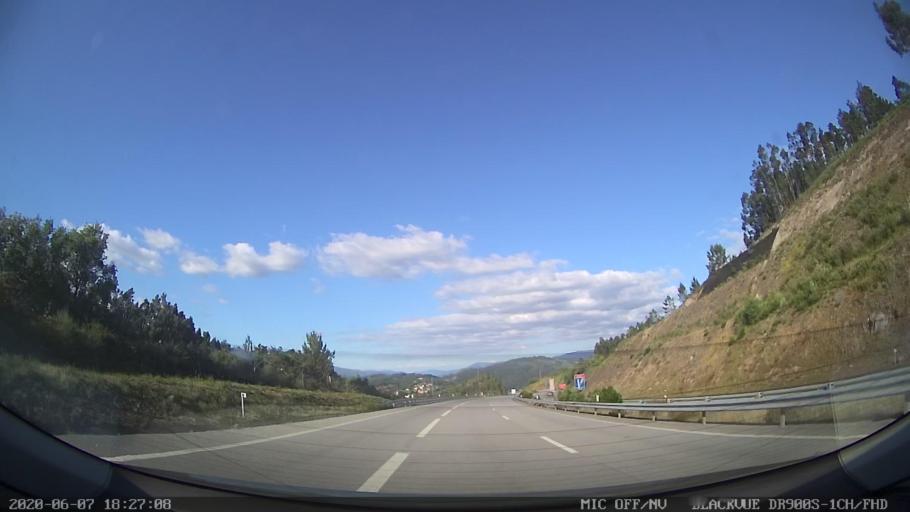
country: PT
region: Braga
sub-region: Cabeceiras de Basto
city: Refojos de Basto
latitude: 41.4535
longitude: -8.0420
